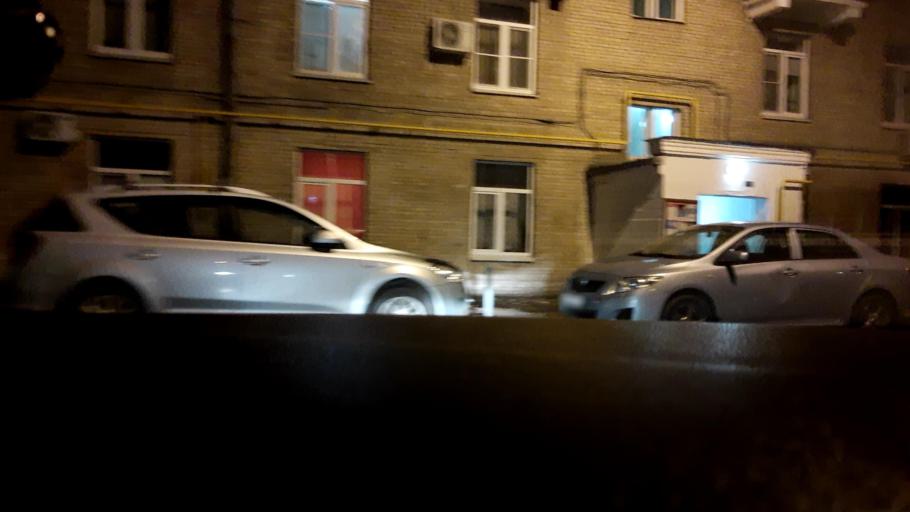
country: RU
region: Moscow
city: Strogino
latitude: 55.8442
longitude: 37.4340
